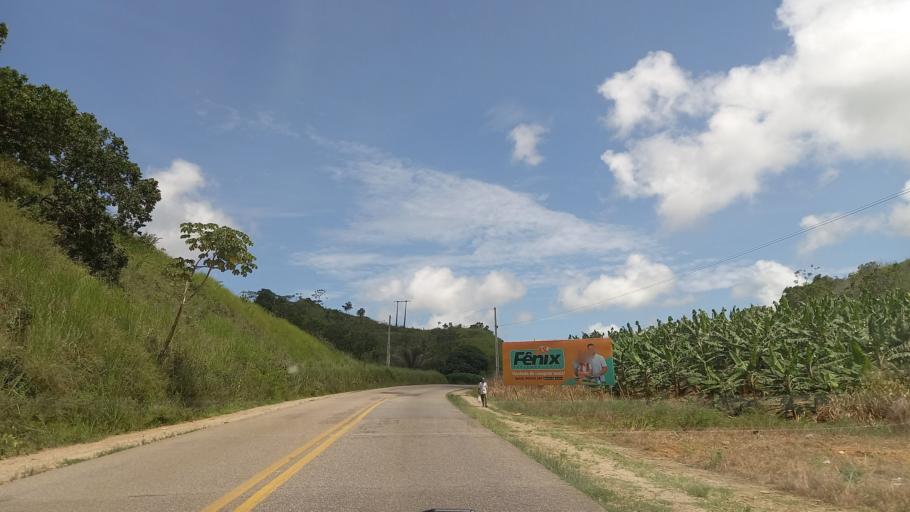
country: BR
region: Pernambuco
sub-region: Barreiros
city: Barreiros
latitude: -8.7865
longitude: -35.1838
